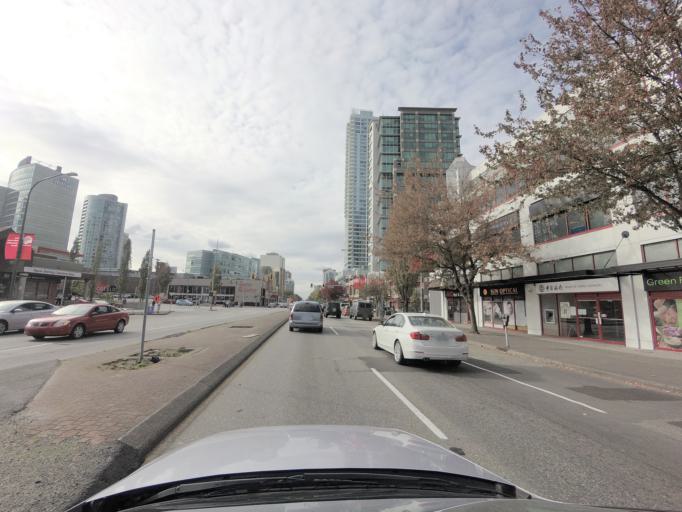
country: CA
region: British Columbia
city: Burnaby
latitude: 49.2297
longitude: -123.0028
